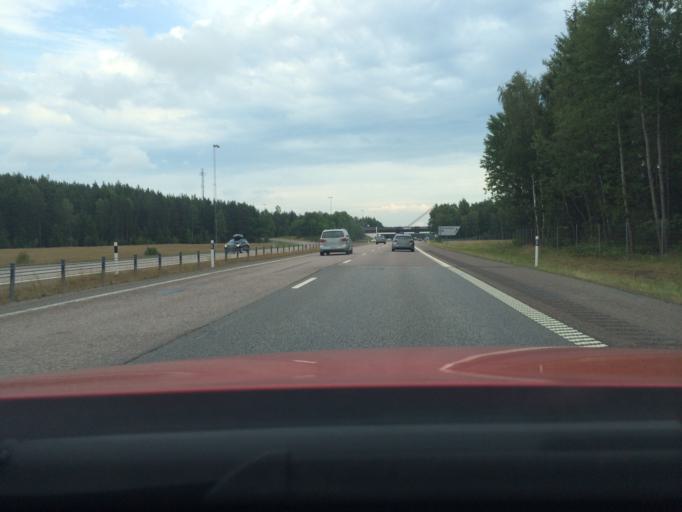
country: SE
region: Soedermanland
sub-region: Nykopings Kommun
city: Svalsta
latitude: 58.7501
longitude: 16.9139
